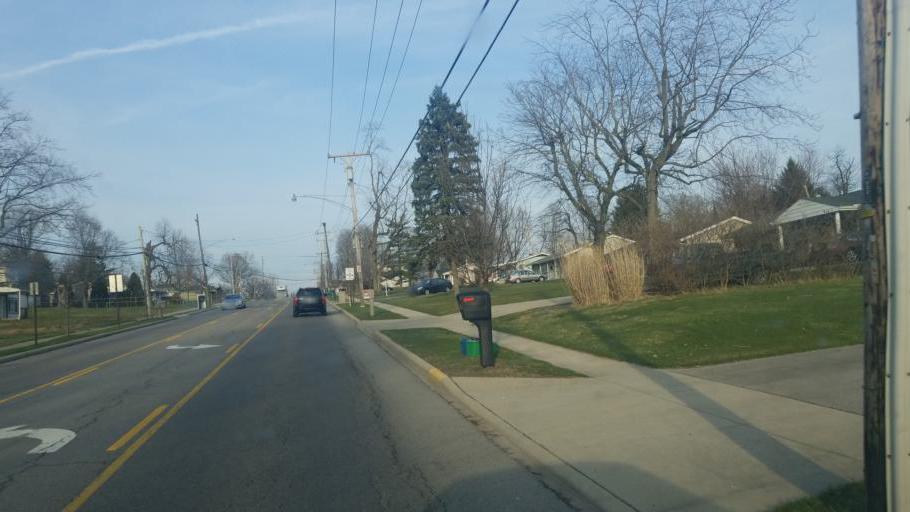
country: US
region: Ohio
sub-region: Logan County
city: Bellefontaine
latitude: 40.3649
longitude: -83.7428
